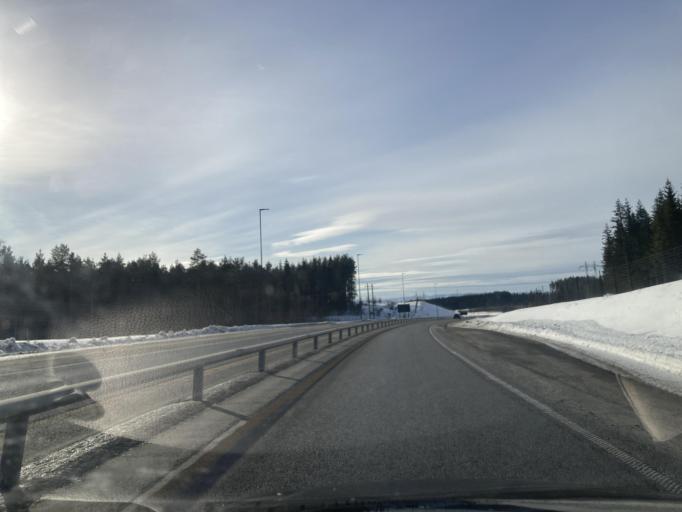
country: NO
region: Hedmark
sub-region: Loten
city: Loten
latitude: 60.8218
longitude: 11.2909
